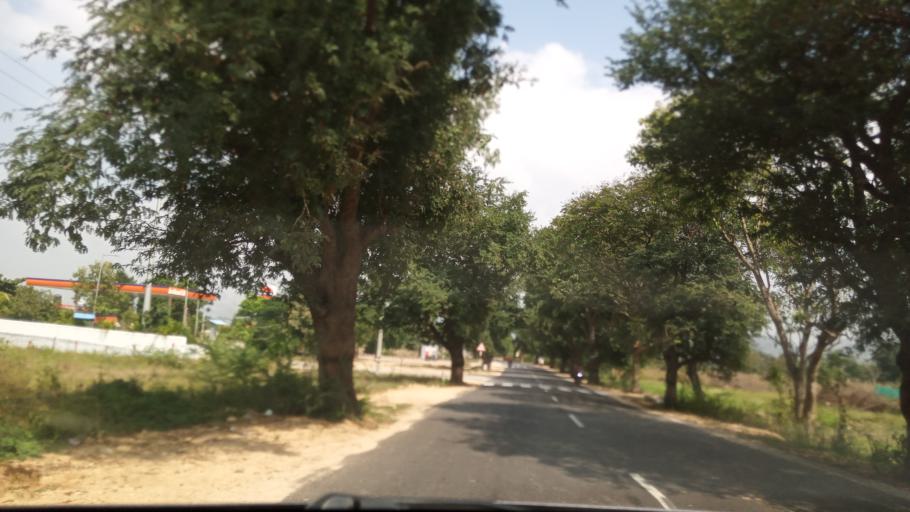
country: IN
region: Andhra Pradesh
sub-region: Chittoor
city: Madanapalle
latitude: 13.6144
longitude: 78.5413
